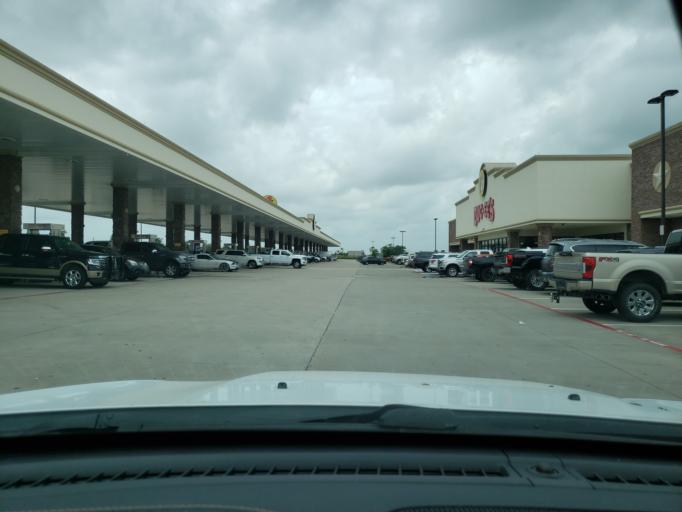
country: US
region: Texas
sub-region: Harris County
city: Katy
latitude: 29.7783
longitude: -95.8468
